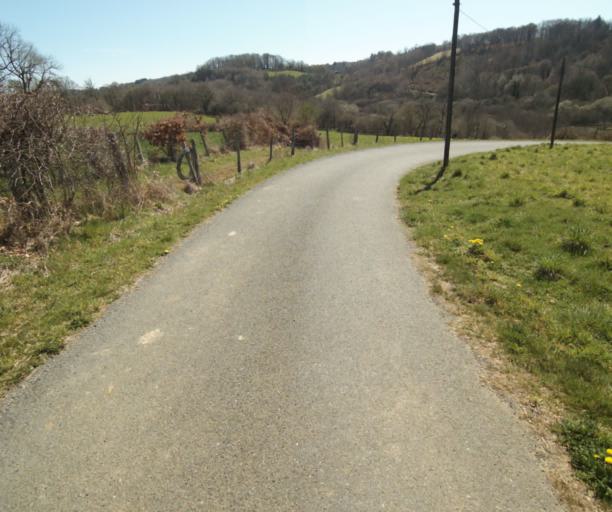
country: FR
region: Limousin
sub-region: Departement de la Correze
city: Chamboulive
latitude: 45.4286
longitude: 1.6808
